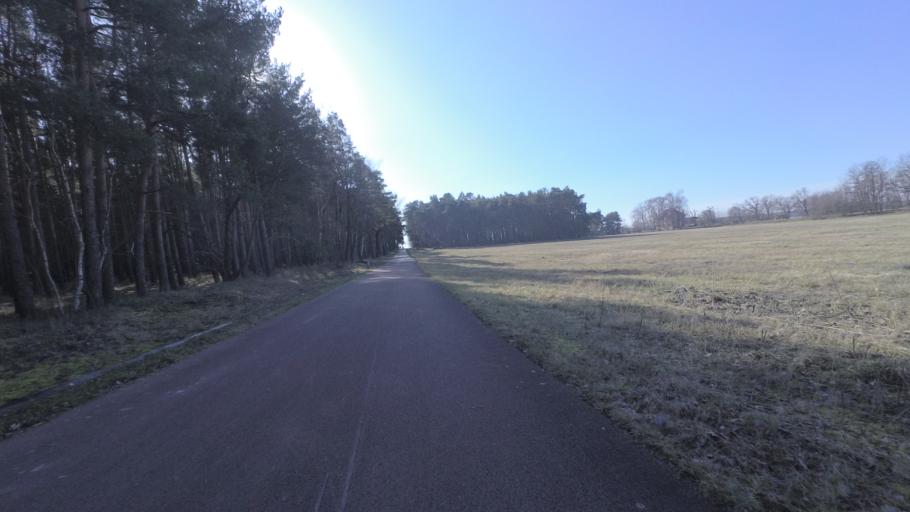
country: DE
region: Brandenburg
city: Juterbog
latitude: 52.0247
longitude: 13.1291
